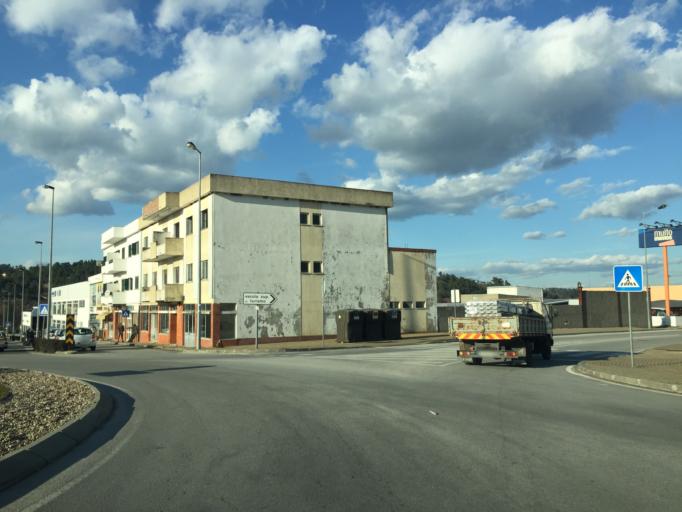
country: PT
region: Guarda
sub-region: Seia
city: Seia
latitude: 40.4278
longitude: -7.7144
